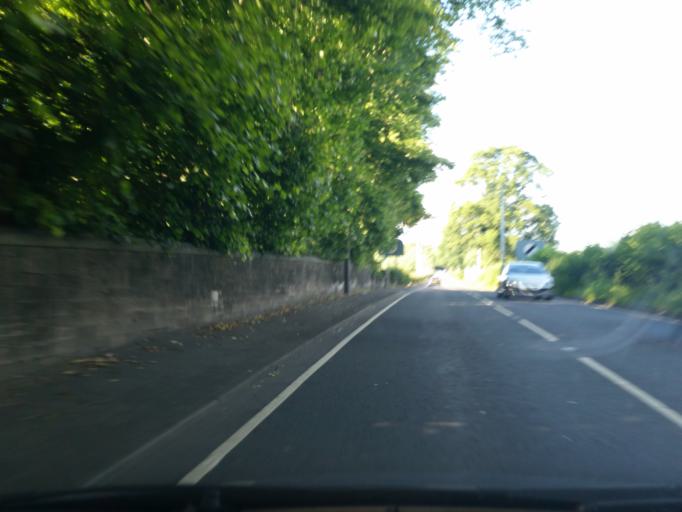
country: GB
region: Scotland
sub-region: South Lanarkshire
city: Dalserf
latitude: 55.7388
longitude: -3.9216
